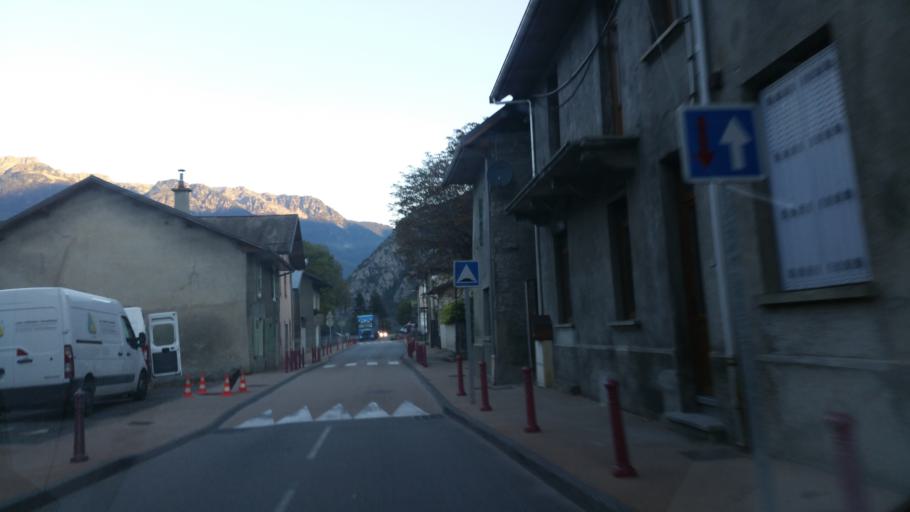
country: FR
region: Rhone-Alpes
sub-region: Departement de la Savoie
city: La Chambre
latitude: 45.3612
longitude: 6.2982
